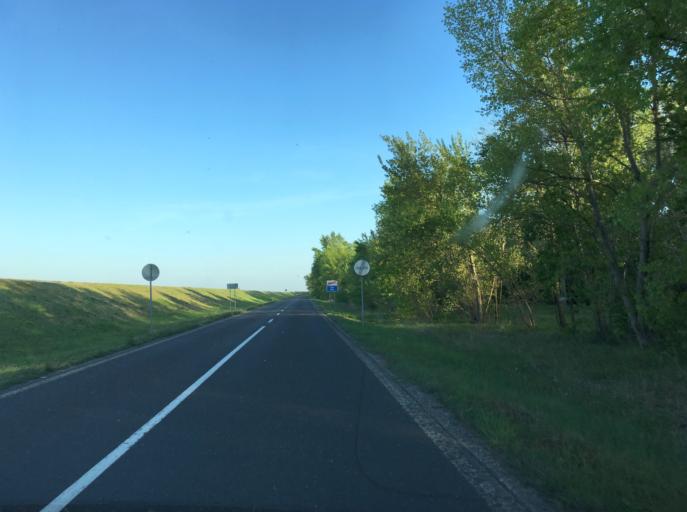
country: HU
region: Gyor-Moson-Sopron
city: Rajka
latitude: 48.0308
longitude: 17.2370
